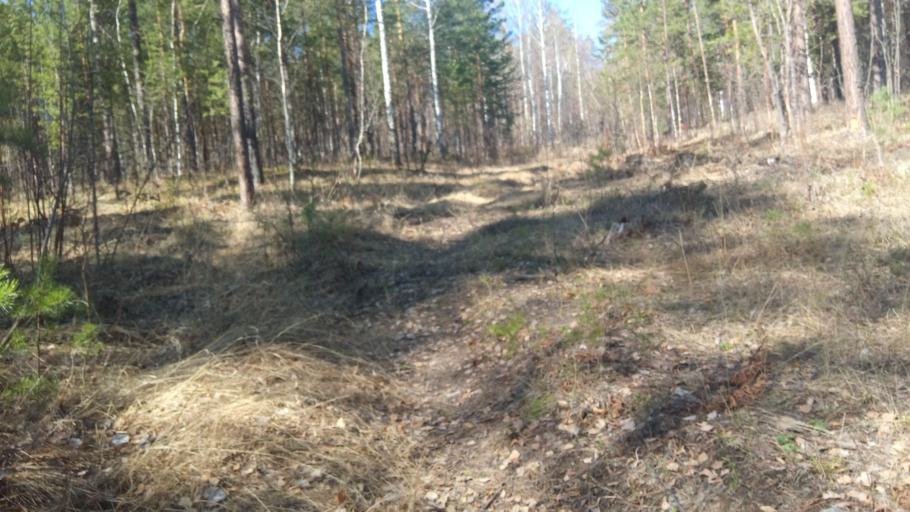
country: RU
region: Chelyabinsk
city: Turgoyak
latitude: 55.1772
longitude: 60.1299
